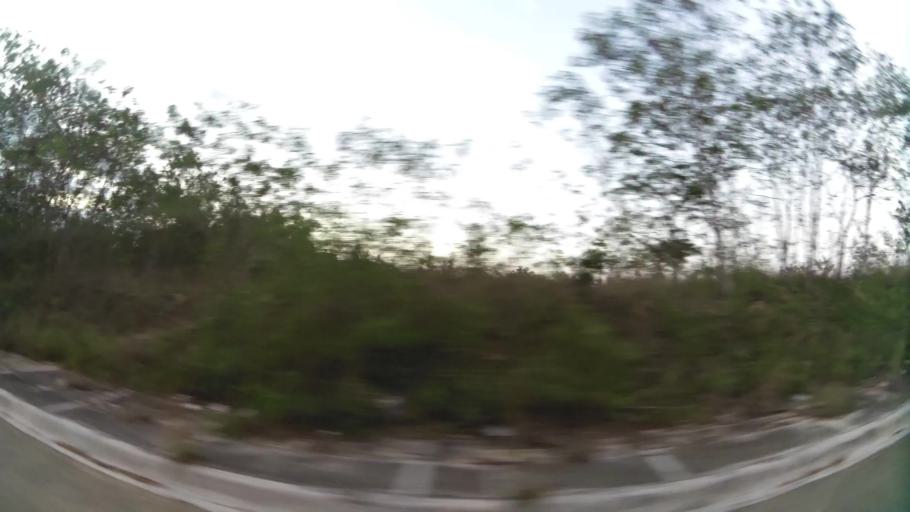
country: DO
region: Nacional
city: La Agustina
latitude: 18.5427
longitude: -69.9479
